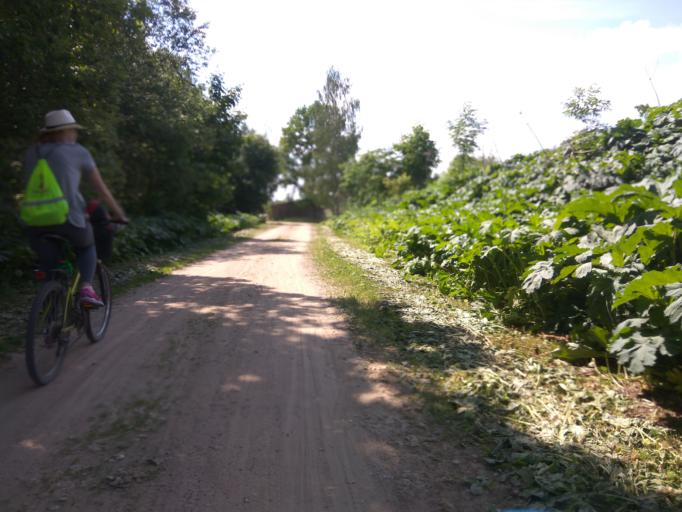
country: LV
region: Kuldigas Rajons
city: Kuldiga
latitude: 56.9227
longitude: 21.9738
